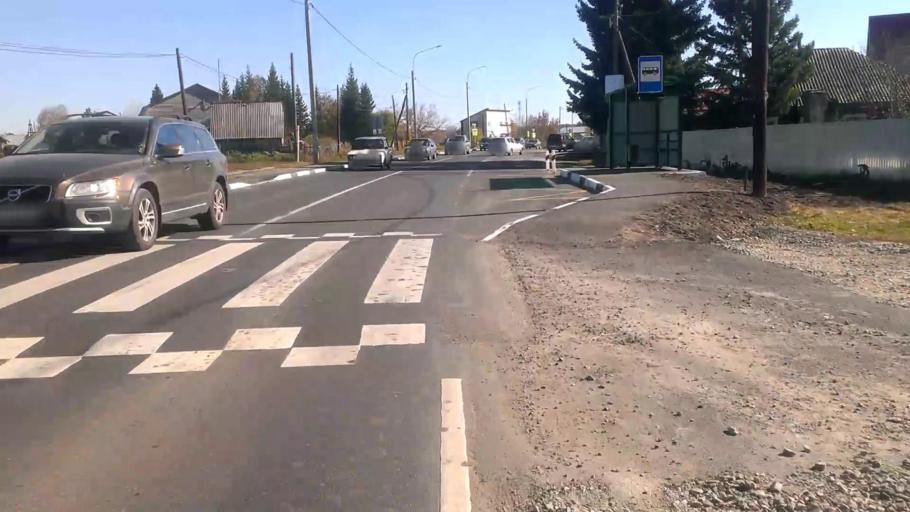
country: RU
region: Altai Krai
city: Sannikovo
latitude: 53.3169
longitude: 83.9563
